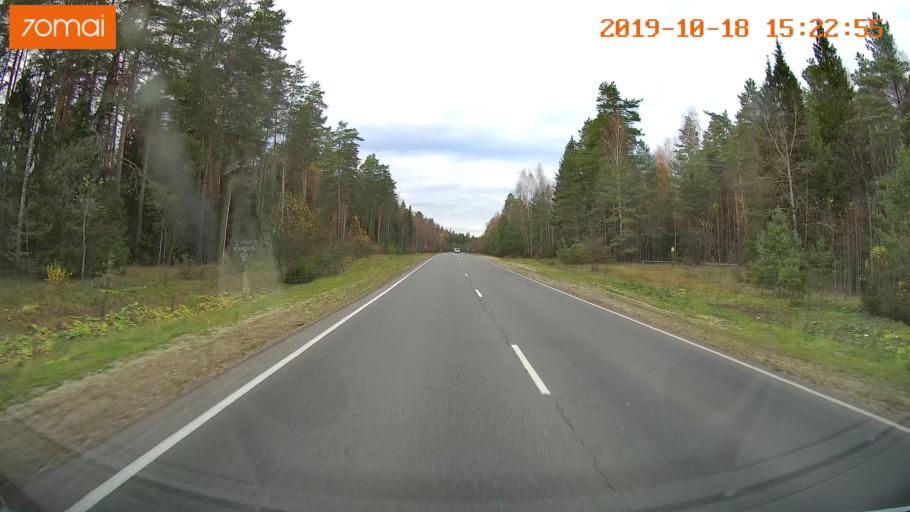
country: RU
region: Vladimir
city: Anopino
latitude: 55.7134
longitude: 40.7273
